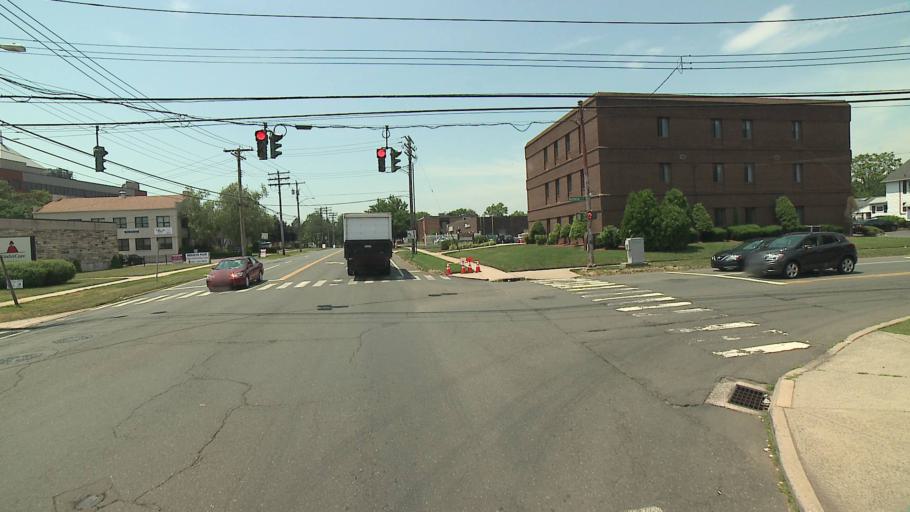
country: US
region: Connecticut
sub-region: New Haven County
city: Hamden
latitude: 41.3832
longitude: -72.8990
